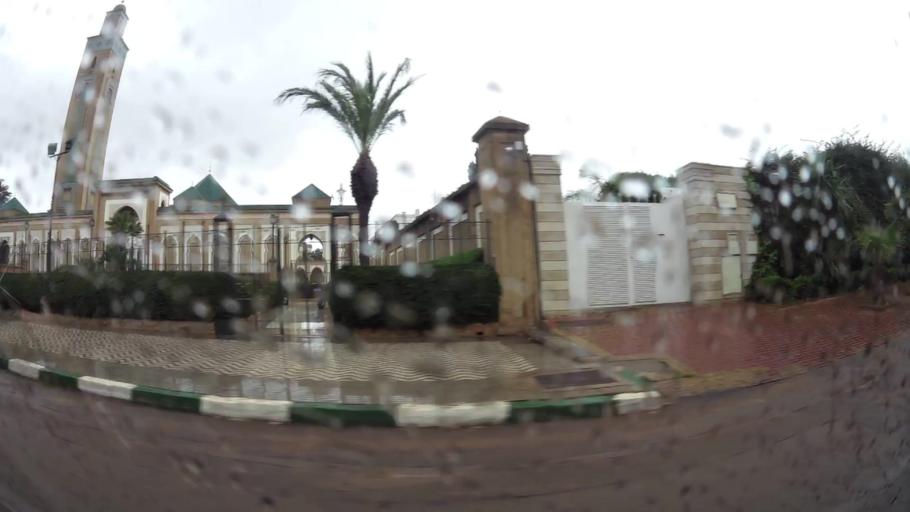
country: MA
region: Grand Casablanca
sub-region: Casablanca
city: Casablanca
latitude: 33.5233
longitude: -7.6316
